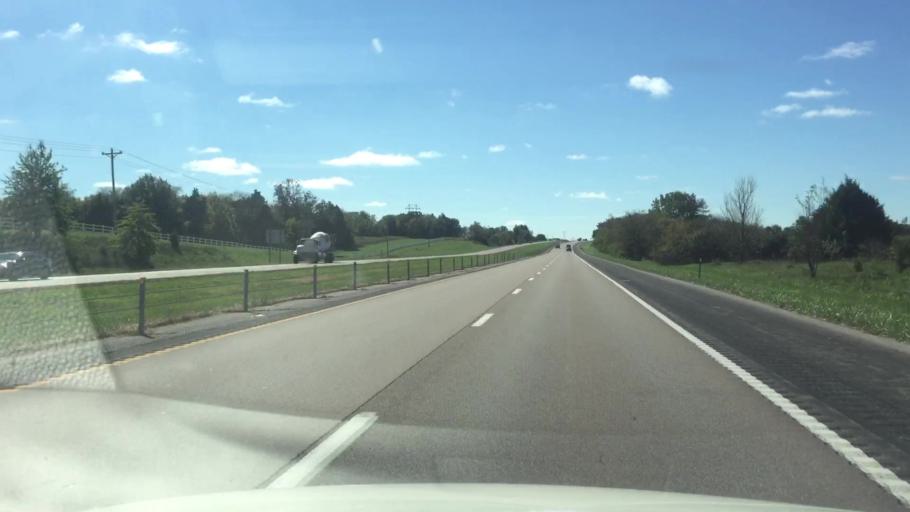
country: US
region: Missouri
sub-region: Boone County
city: Ashland
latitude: 38.8074
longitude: -92.2515
